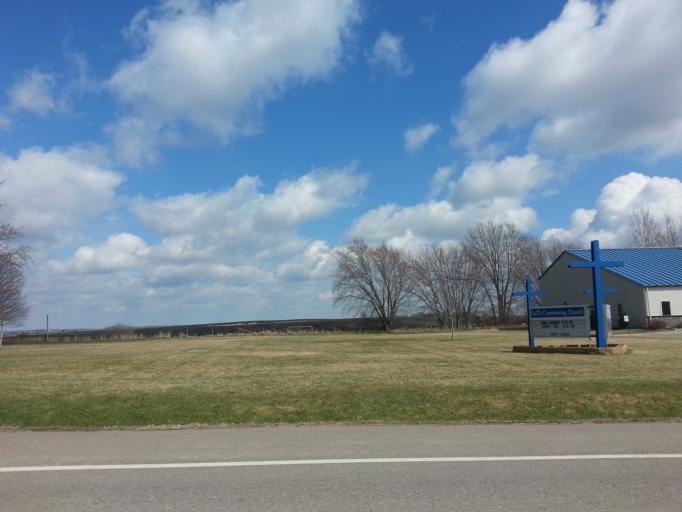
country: US
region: Minnesota
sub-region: Dodge County
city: Dodge Center
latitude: 44.1574
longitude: -92.8993
